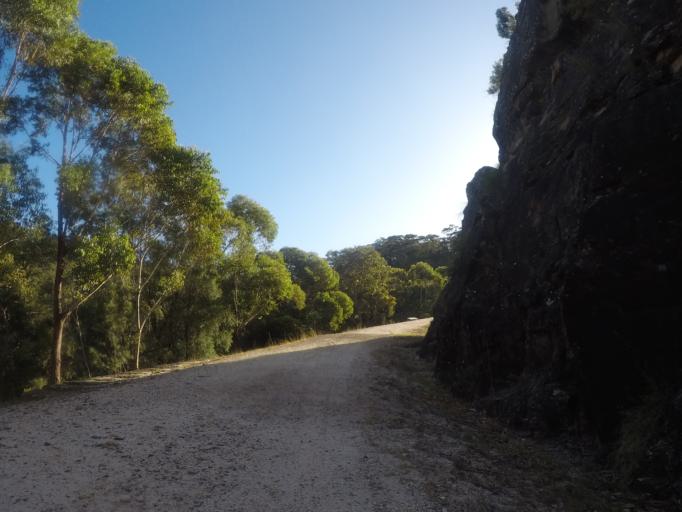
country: AU
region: New South Wales
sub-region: Hornsby Shire
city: Glenorie
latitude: -33.3690
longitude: 150.9856
